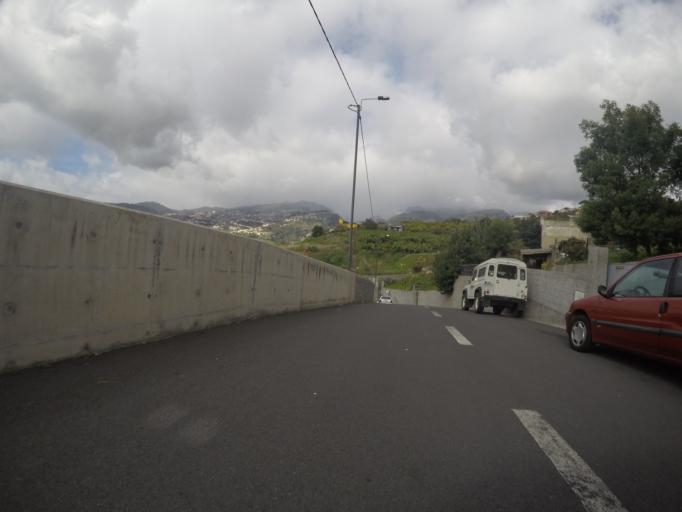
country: PT
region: Madeira
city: Camara de Lobos
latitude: 32.6496
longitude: -16.9519
